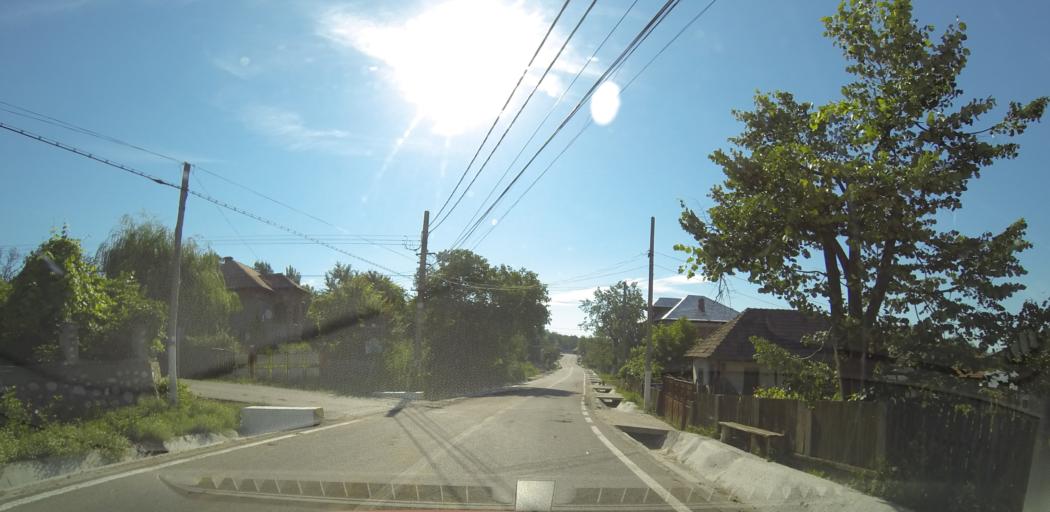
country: RO
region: Valcea
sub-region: Comuna Vaideeni
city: Vaideeni
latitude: 45.1680
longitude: 23.9011
